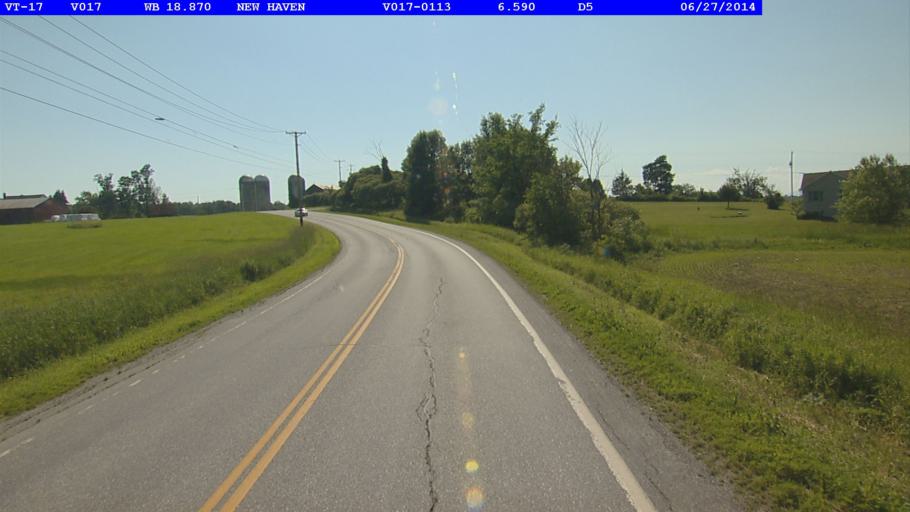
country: US
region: Vermont
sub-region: Addison County
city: Bristol
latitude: 44.1272
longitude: -73.1204
